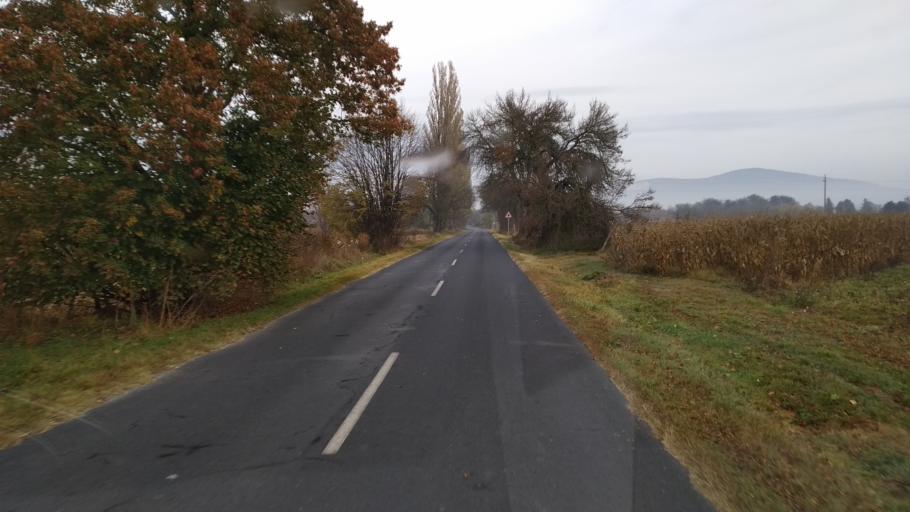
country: HU
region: Pest
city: Tahitotfalu
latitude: 47.7648
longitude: 19.0864
